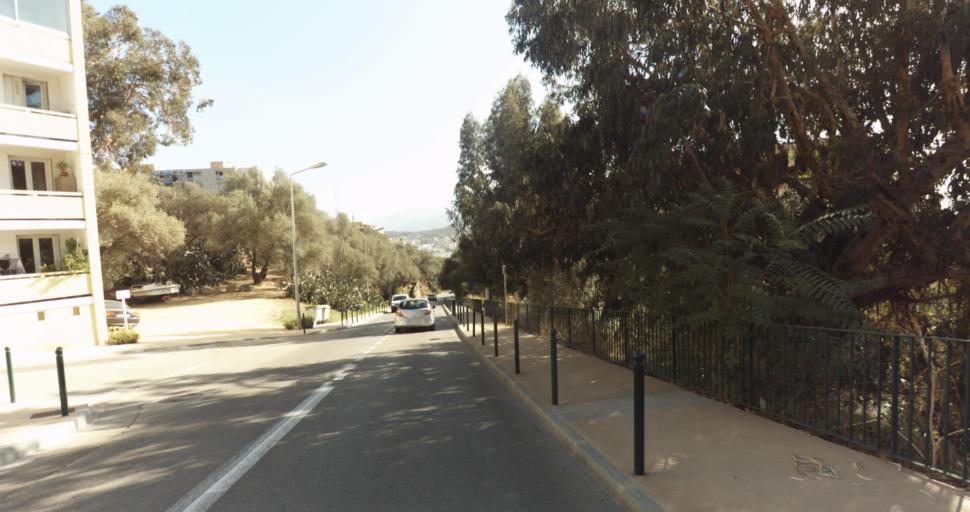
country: FR
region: Corsica
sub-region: Departement de la Corse-du-Sud
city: Ajaccio
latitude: 41.9269
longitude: 8.7298
